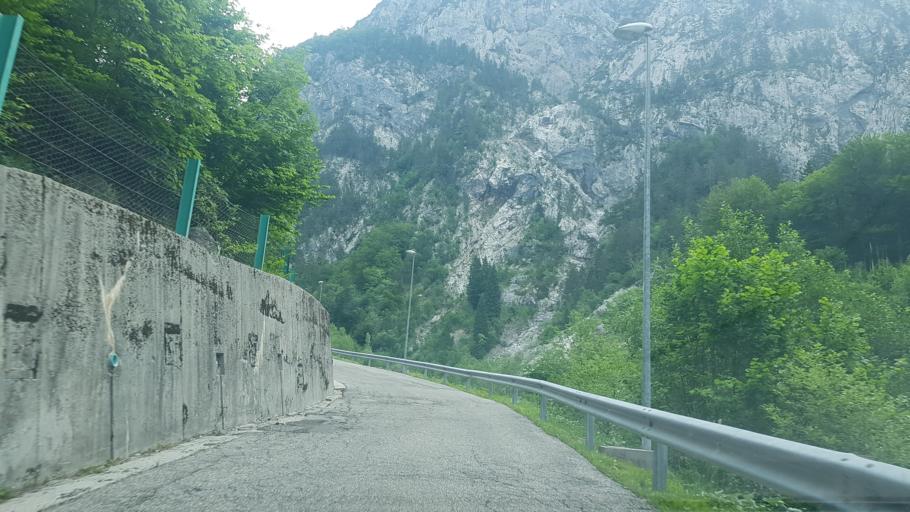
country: IT
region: Friuli Venezia Giulia
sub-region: Provincia di Udine
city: Pontebba
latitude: 46.5308
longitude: 13.3057
